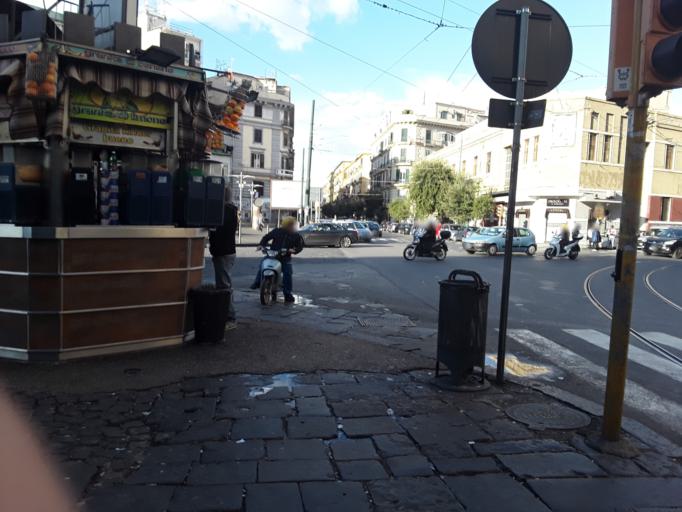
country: IT
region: Campania
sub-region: Provincia di Napoli
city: Napoli
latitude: 40.8551
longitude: 14.2675
